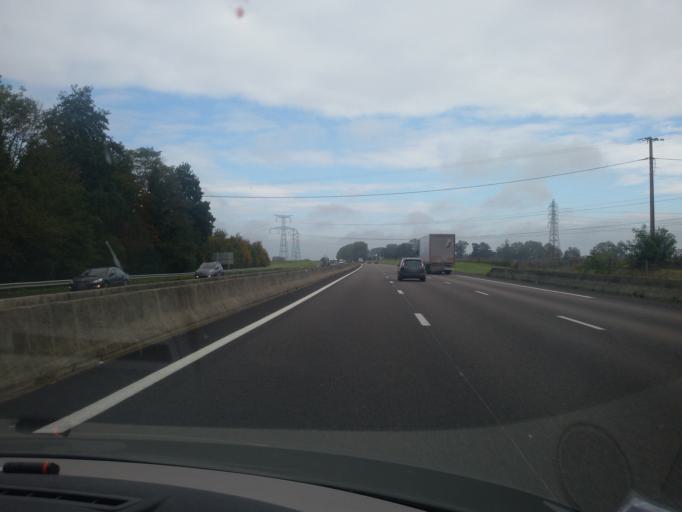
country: FR
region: Haute-Normandie
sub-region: Departement de l'Eure
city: Hauville
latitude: 49.3698
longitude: 0.7397
